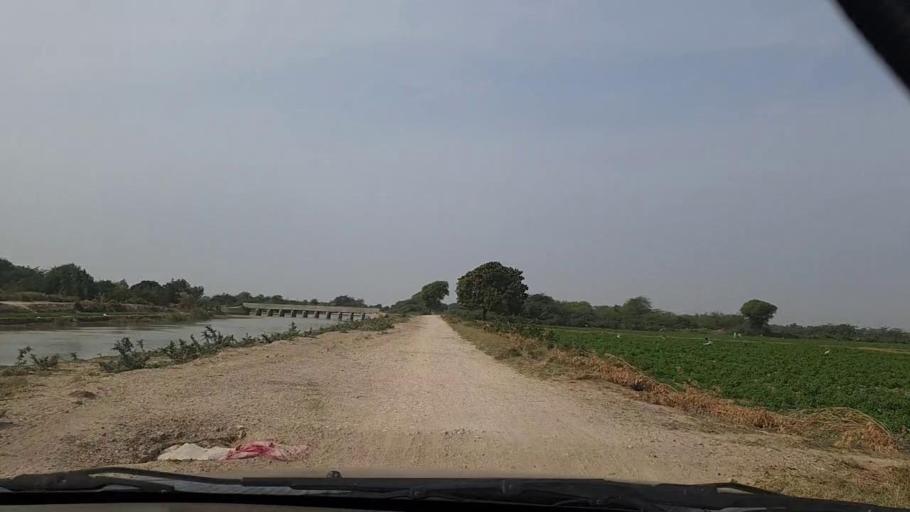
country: PK
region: Sindh
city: Thatta
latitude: 24.5725
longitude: 67.8530
